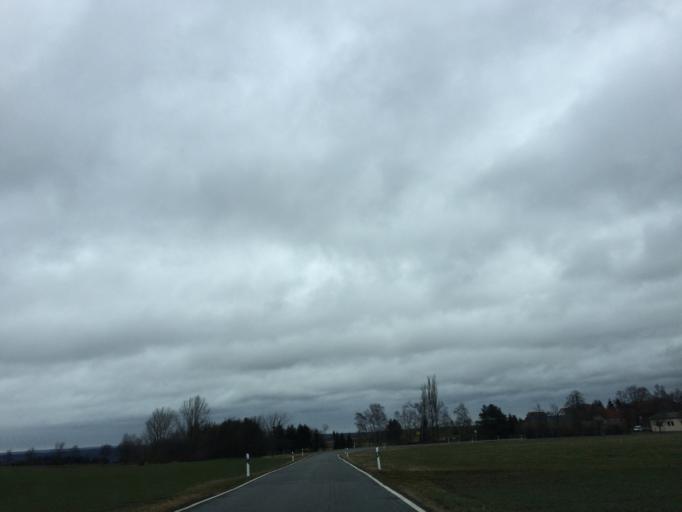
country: DE
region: Thuringia
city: Peuschen
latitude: 50.6573
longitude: 11.6372
